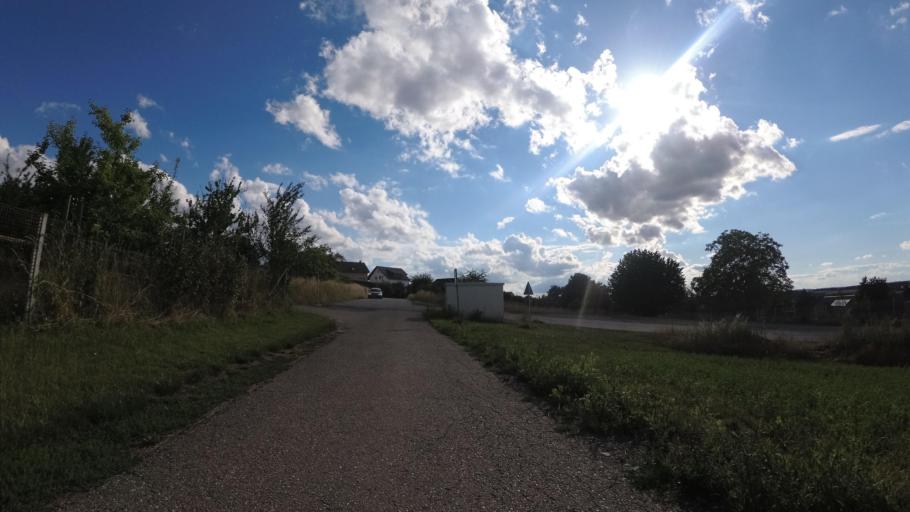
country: DE
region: Baden-Wuerttemberg
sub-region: Regierungsbezirk Stuttgart
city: Oedheim
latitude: 49.2402
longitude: 9.2670
